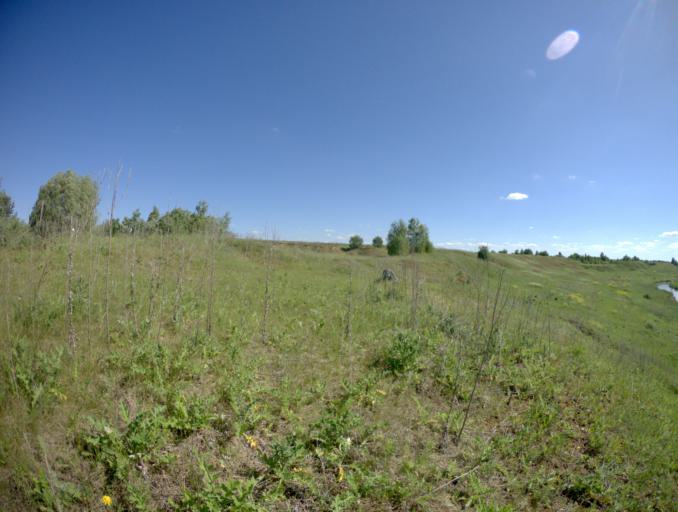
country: RU
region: Ivanovo
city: Gavrilov Posad
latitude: 56.5270
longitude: 40.2064
